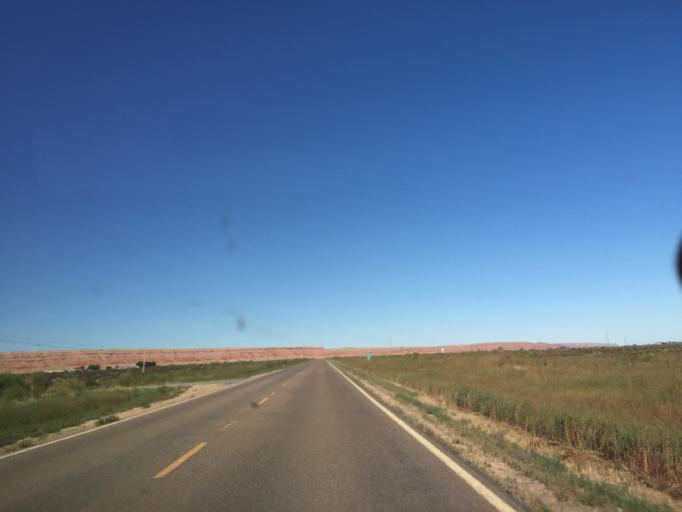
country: US
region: Arizona
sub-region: Apache County
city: Many Farms
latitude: 36.3288
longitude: -109.6209
